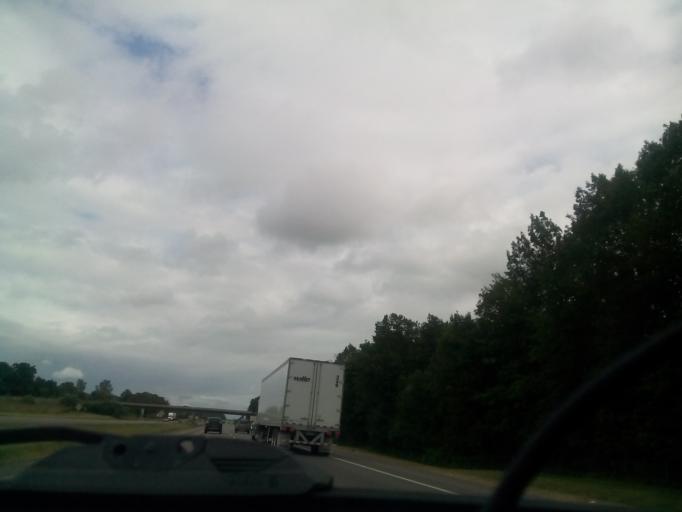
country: US
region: Ohio
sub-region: Williams County
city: Montpelier
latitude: 41.6280
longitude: -84.7311
